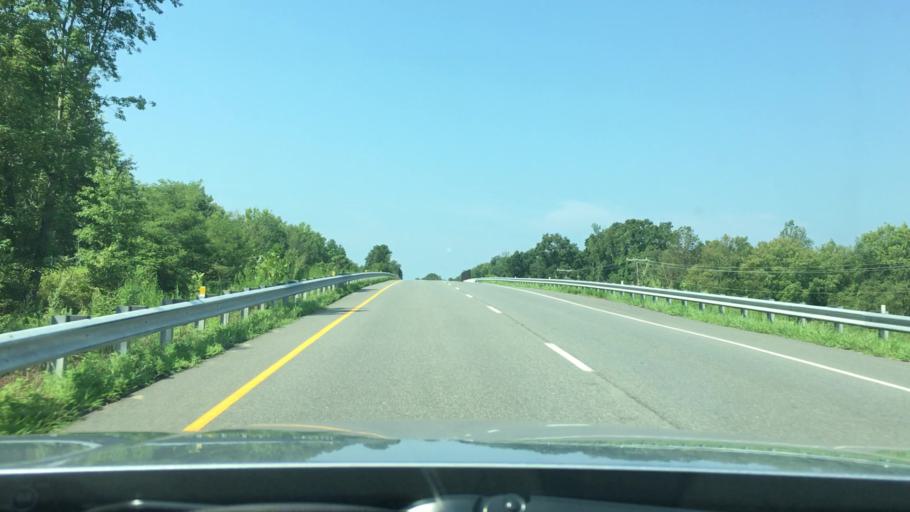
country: US
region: Virginia
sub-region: Caroline County
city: Bowling Green
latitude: 38.0335
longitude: -77.3740
